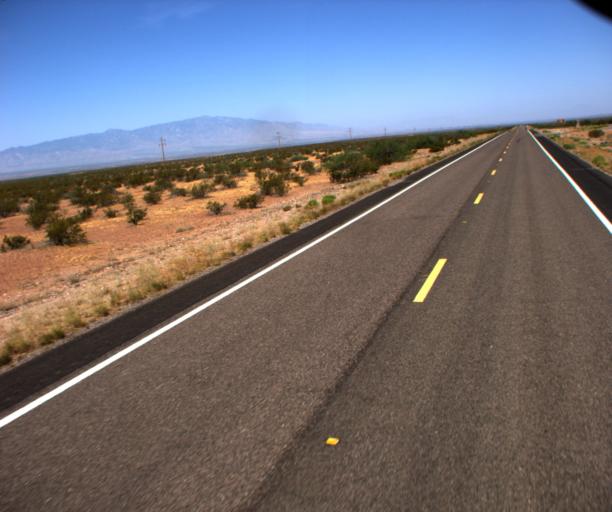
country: US
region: Arizona
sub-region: Graham County
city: Swift Trail Junction
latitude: 32.7600
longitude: -109.4378
